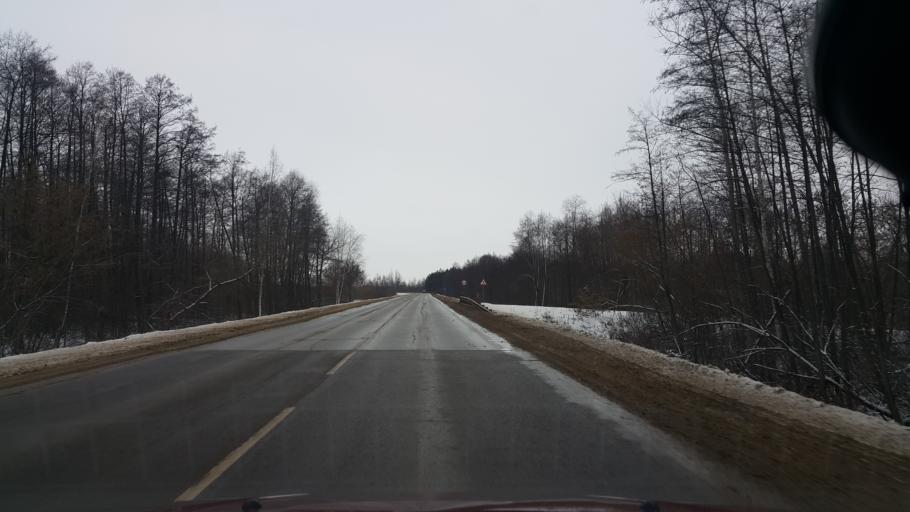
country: RU
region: Tambov
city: Kotovsk
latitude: 52.6299
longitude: 41.5068
